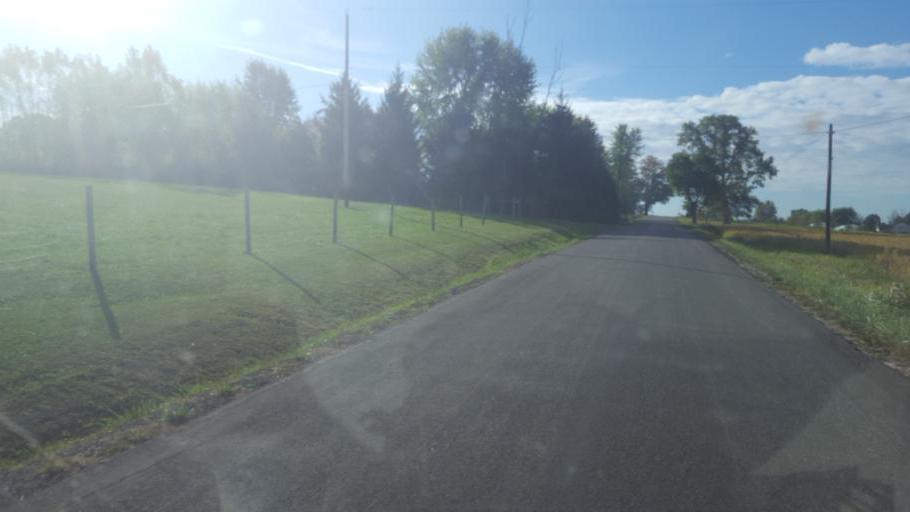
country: US
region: Pennsylvania
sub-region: Mercer County
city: Mercer
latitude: 41.3537
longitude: -80.2462
